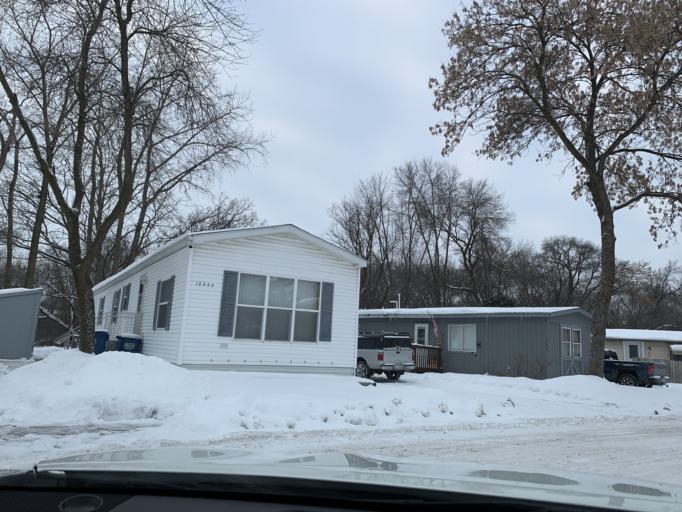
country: US
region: Minnesota
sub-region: Anoka County
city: Coon Rapids
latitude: 45.1593
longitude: -93.2961
